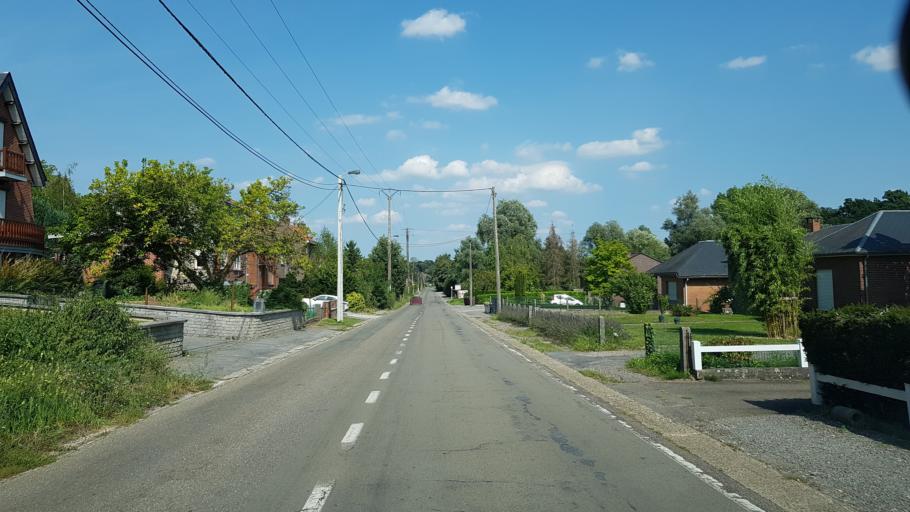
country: BE
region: Wallonia
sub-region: Province de Liege
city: Dalhem
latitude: 50.7006
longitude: 5.7031
